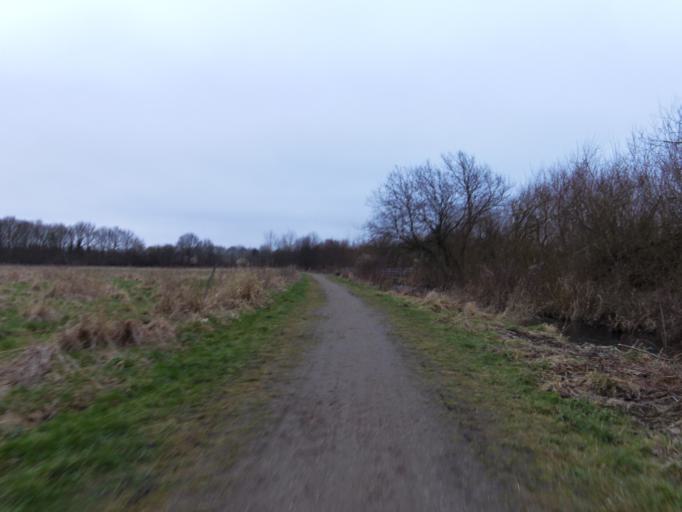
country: DK
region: South Denmark
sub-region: Odense Kommune
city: Neder Holluf
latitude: 55.3811
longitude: 10.4410
